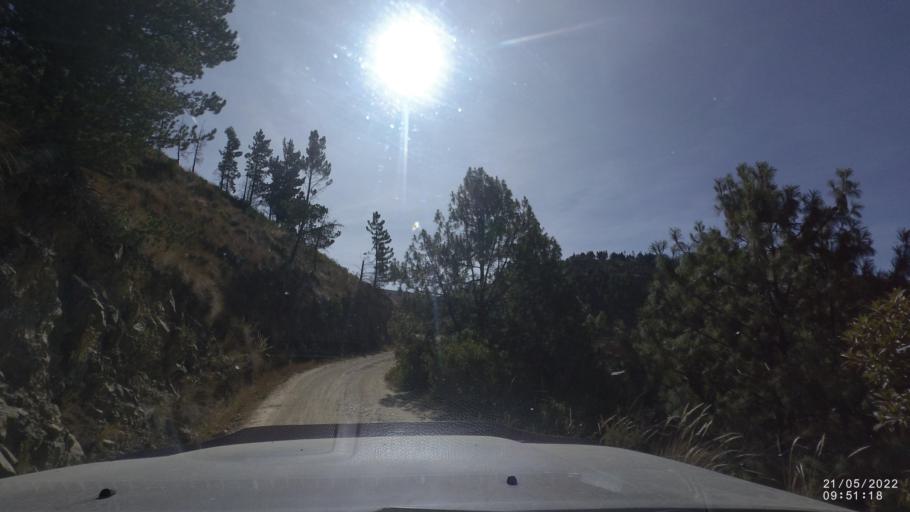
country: BO
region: Cochabamba
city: Colomi
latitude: -17.3424
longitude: -65.9910
